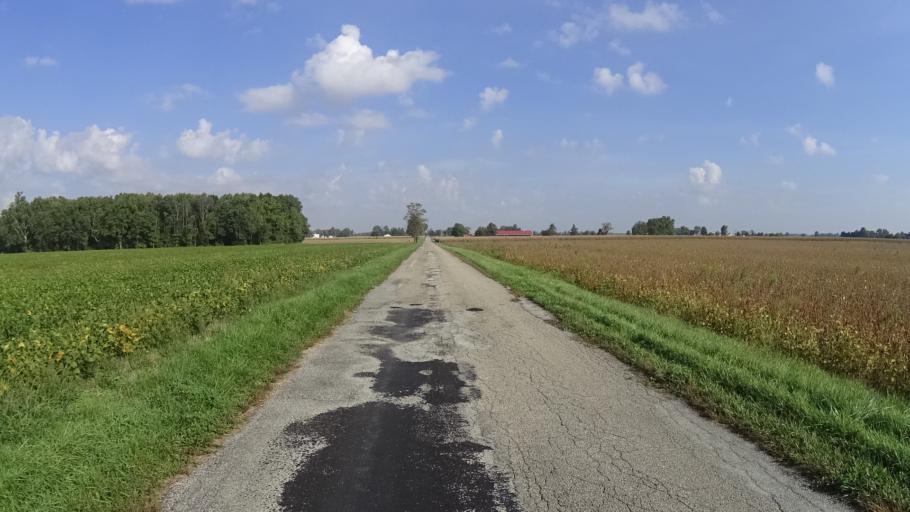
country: US
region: Indiana
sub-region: Madison County
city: Ingalls
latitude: 40.0058
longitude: -85.8243
